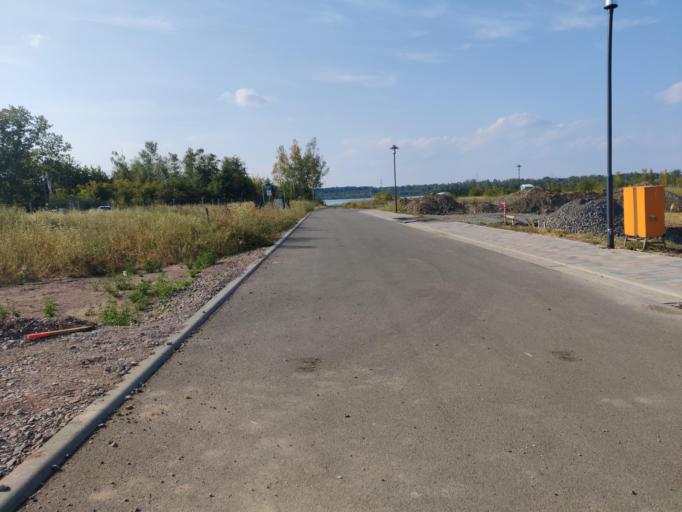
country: DE
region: Saxony
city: Neukieritzsch
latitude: 51.1696
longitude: 12.4345
